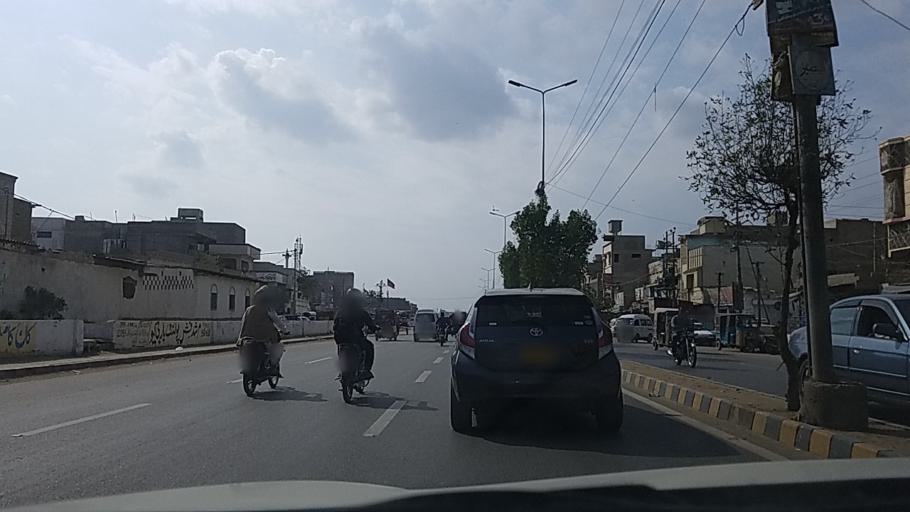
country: PK
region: Sindh
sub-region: Karachi District
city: Karachi
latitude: 24.8218
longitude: 67.1319
